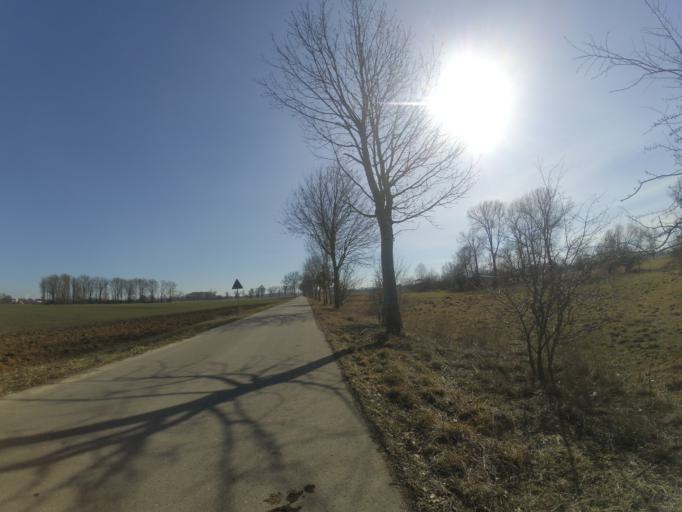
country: DE
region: Baden-Wuerttemberg
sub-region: Tuebingen Region
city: Rammingen
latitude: 48.5001
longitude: 10.1521
